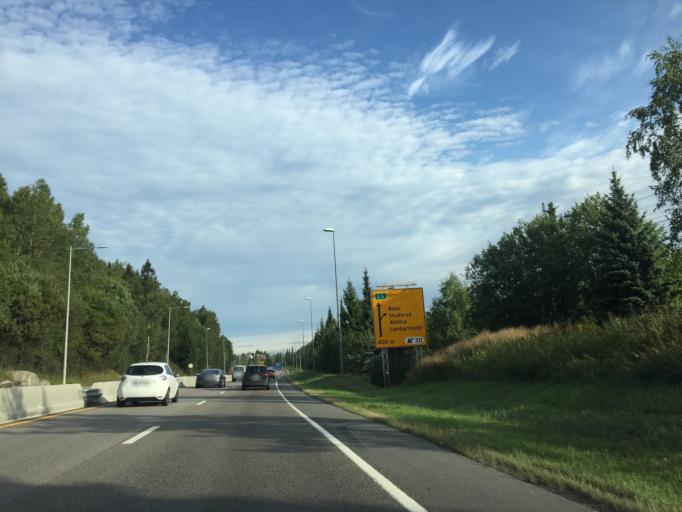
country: NO
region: Akershus
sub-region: Oppegard
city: Kolbotn
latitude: 59.8725
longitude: 10.8257
